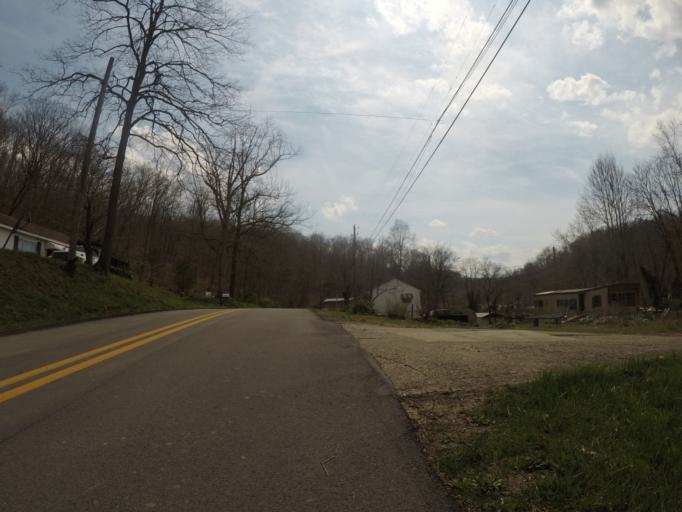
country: US
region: West Virginia
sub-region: Cabell County
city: Pea Ridge
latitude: 38.4040
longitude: -82.3490
